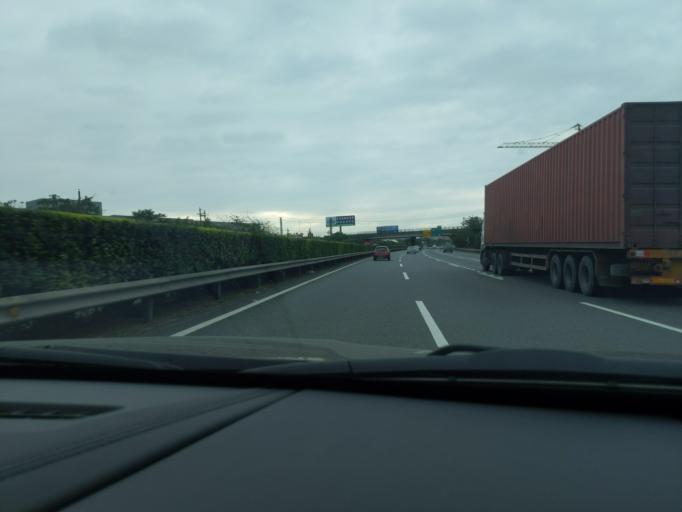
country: CN
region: Fujian
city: Neikeng
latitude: 24.7532
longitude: 118.4420
